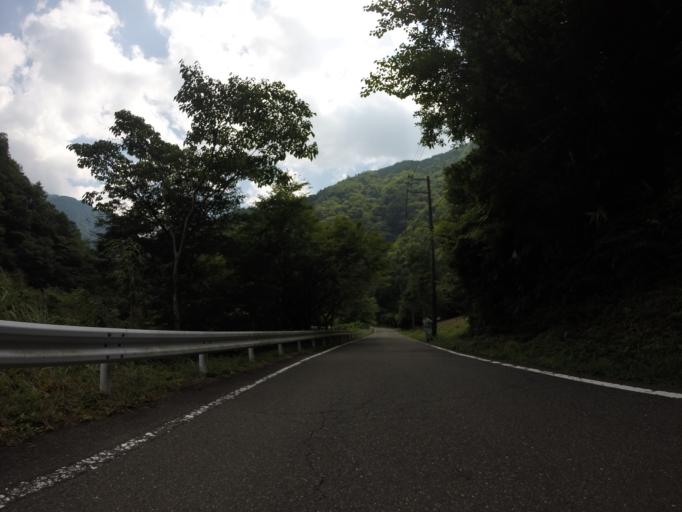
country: JP
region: Shizuoka
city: Fujinomiya
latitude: 35.2908
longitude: 138.3361
